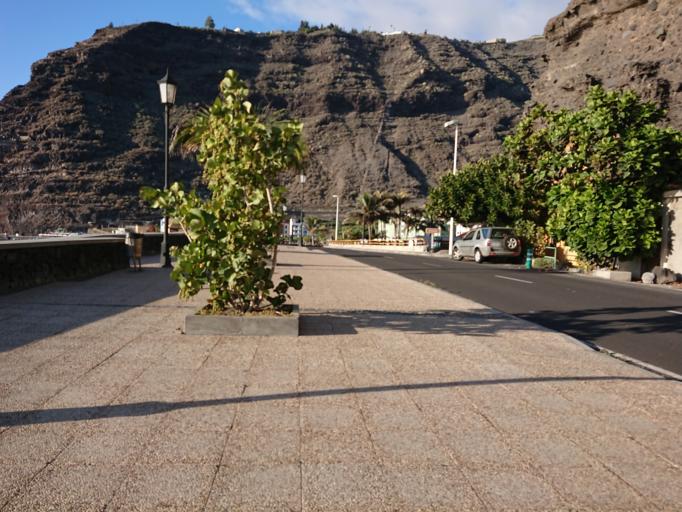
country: ES
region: Canary Islands
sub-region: Provincia de Santa Cruz de Tenerife
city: Tazacorte
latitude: 28.6494
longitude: -17.9452
